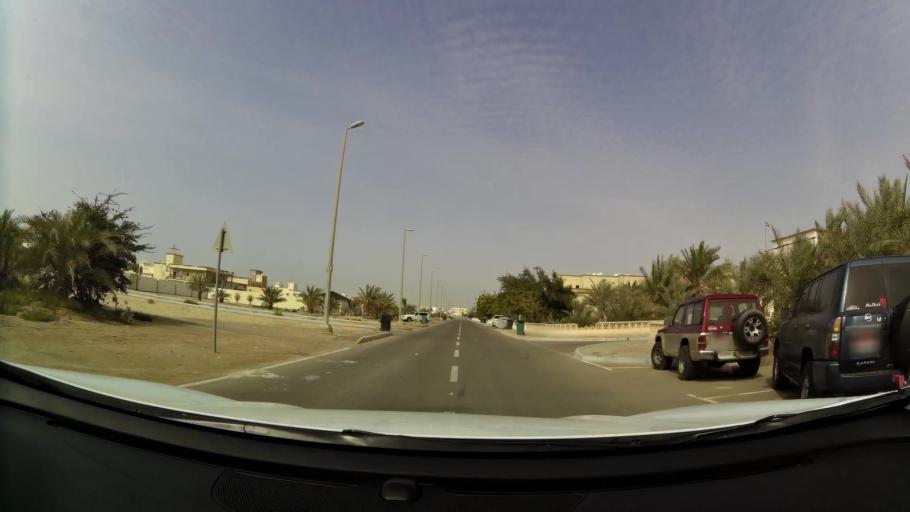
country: AE
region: Abu Dhabi
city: Abu Dhabi
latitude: 24.5775
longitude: 54.6873
